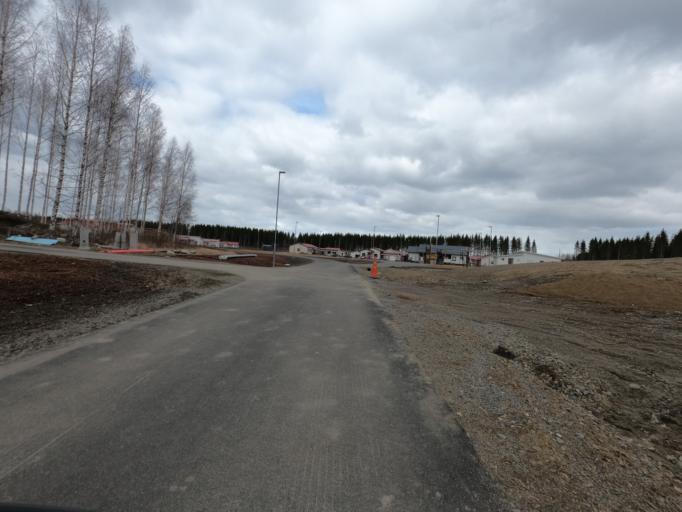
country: FI
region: North Karelia
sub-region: Joensuu
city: Joensuu
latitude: 62.5574
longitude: 29.8262
